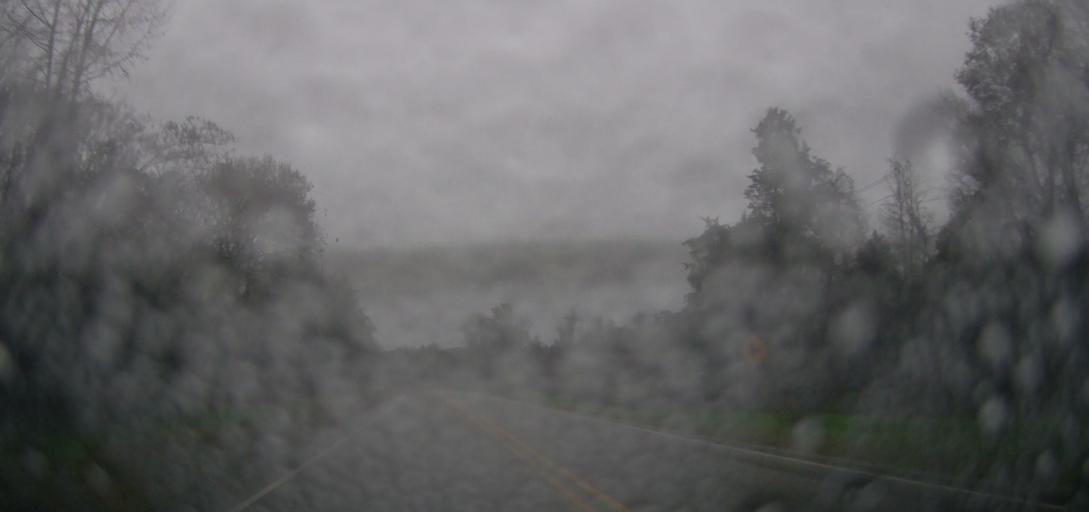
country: US
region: Alabama
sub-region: Autauga County
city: Prattville
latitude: 32.4929
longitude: -86.5754
